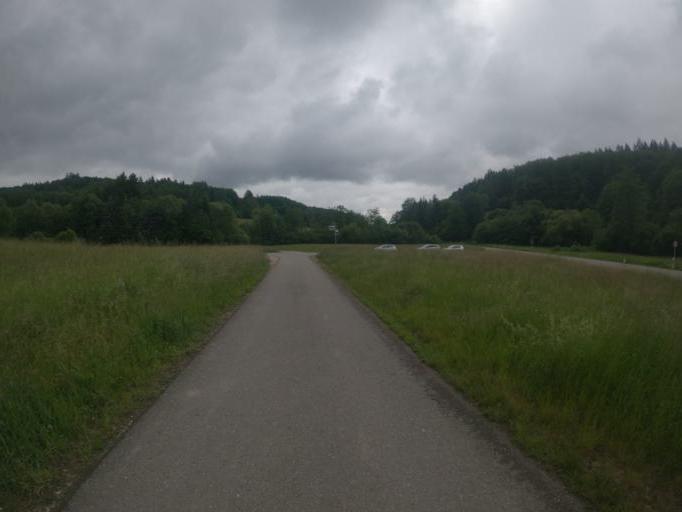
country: DE
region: Baden-Wuerttemberg
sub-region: Regierungsbezirk Stuttgart
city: Ebersbach an der Fils
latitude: 48.7505
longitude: 9.5375
